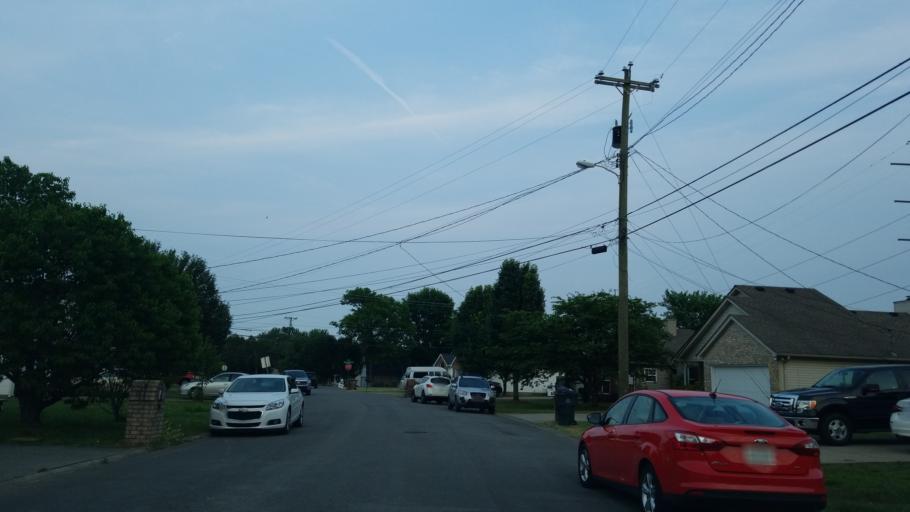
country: US
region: Tennessee
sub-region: Rutherford County
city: La Vergne
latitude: 36.0310
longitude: -86.5899
